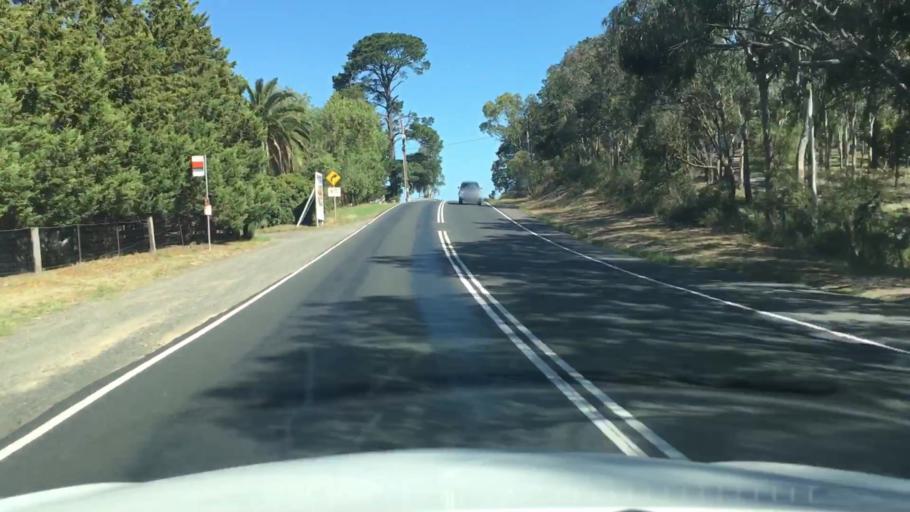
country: AU
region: Victoria
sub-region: Nillumbik
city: North Warrandyte
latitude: -37.6983
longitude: 145.2245
